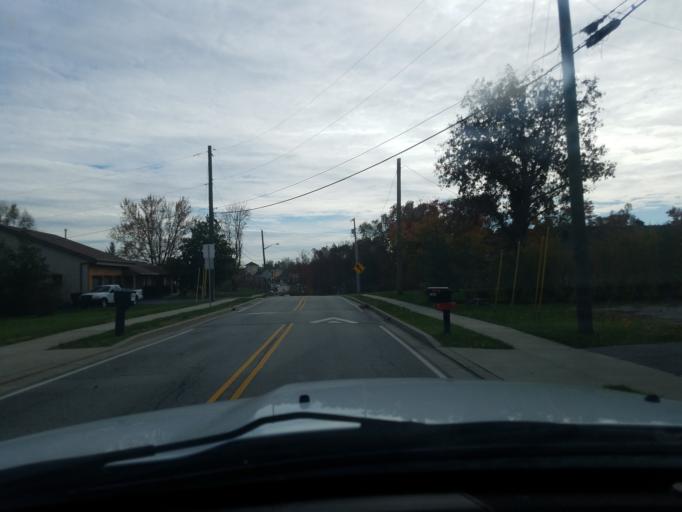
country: US
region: Indiana
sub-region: Floyd County
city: New Albany
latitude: 38.3369
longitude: -85.8021
